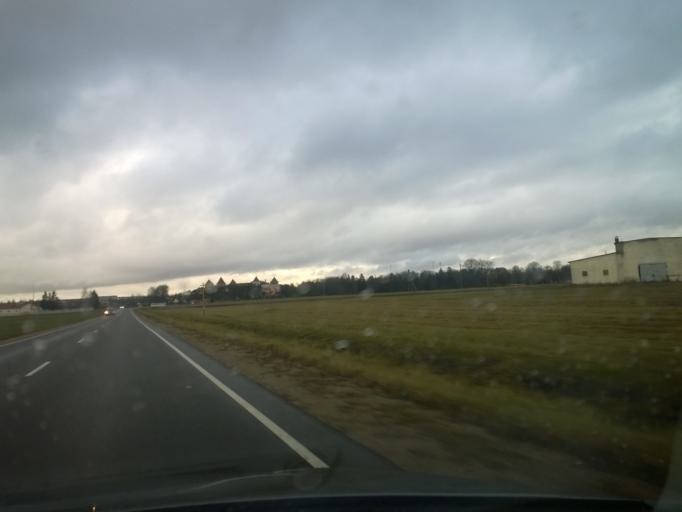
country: BY
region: Grodnenskaya
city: Mir
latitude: 53.4447
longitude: 26.4754
